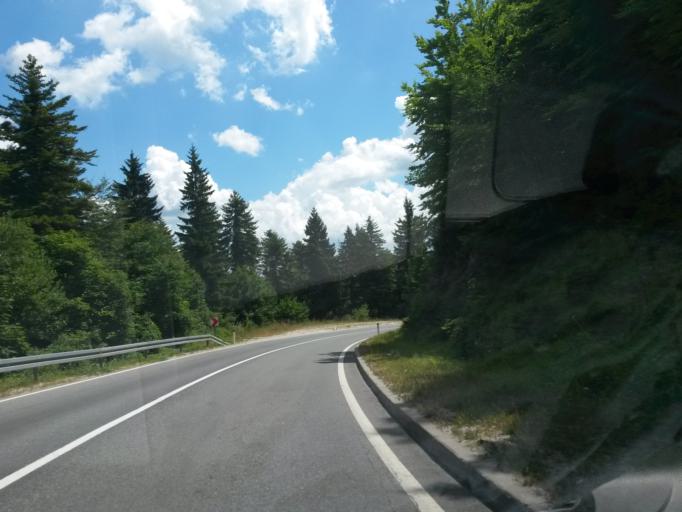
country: BA
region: Federation of Bosnia and Herzegovina
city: Bugojno
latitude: 44.0259
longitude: 17.3008
